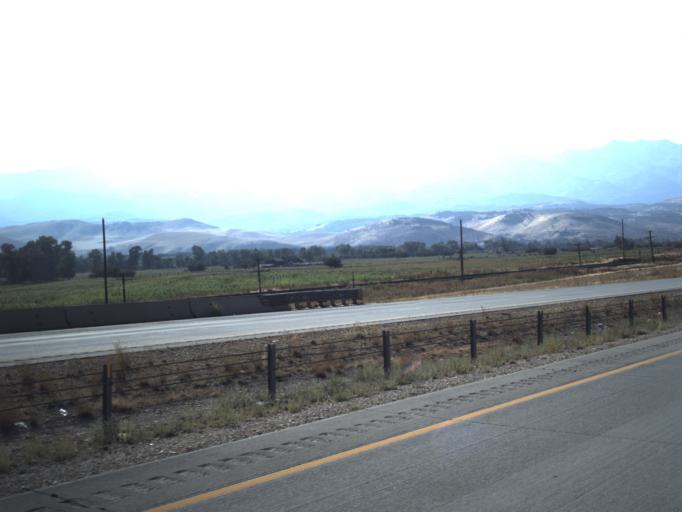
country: US
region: Utah
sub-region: Morgan County
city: Morgan
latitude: 41.0555
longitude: -111.6932
